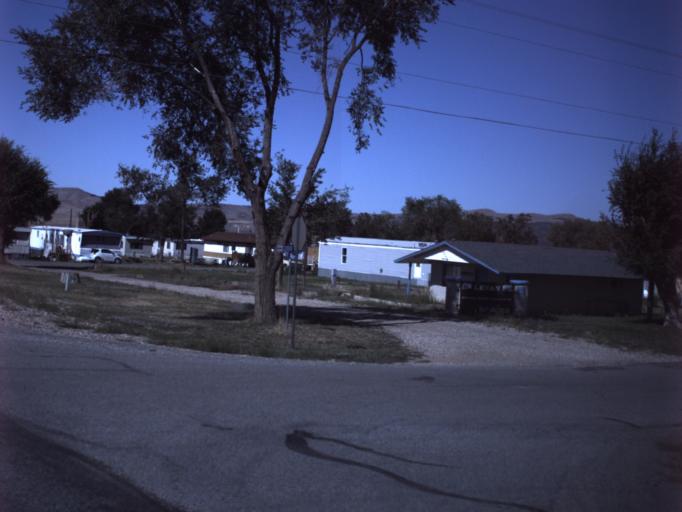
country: US
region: Utah
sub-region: Juab County
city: Nephi
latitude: 39.5588
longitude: -111.8676
